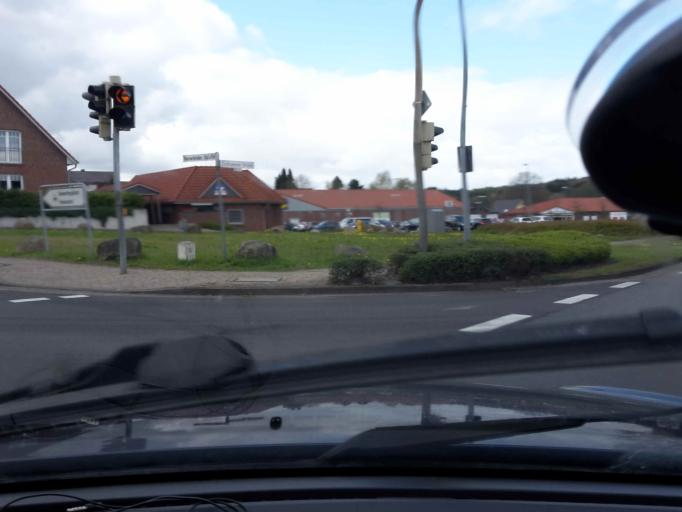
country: DE
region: Lower Saxony
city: Nottensdorf
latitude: 53.4835
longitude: 9.6240
